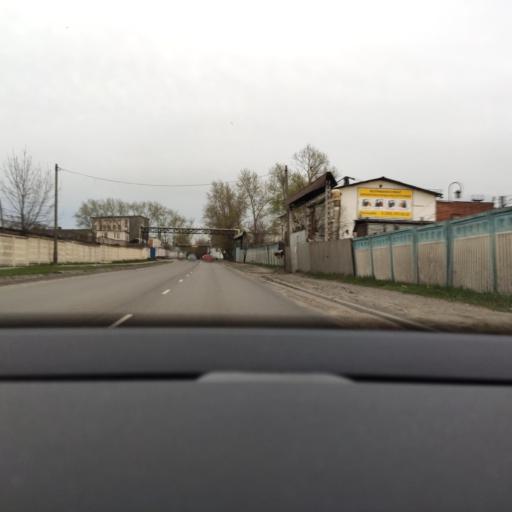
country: RU
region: Moskovskaya
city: Reutov
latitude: 55.7741
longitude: 37.8687
